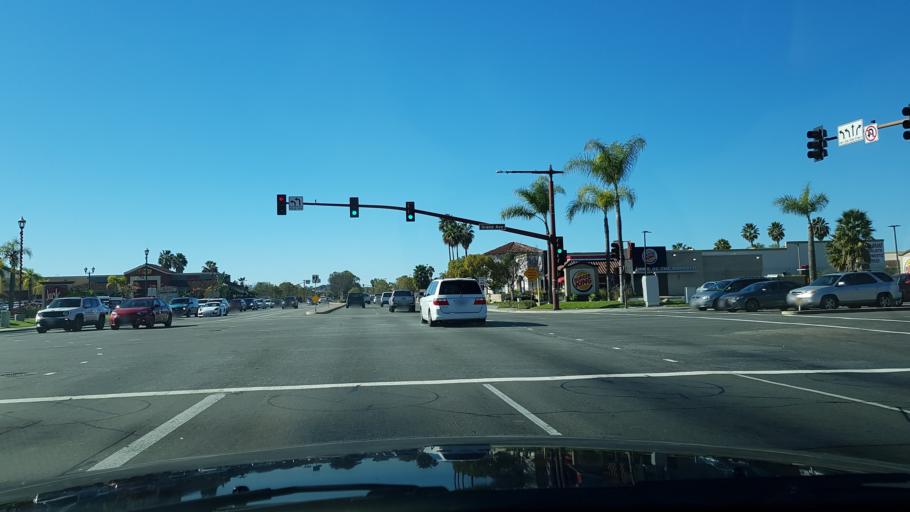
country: US
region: California
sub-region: San Diego County
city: San Marcos
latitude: 33.1373
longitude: -117.1787
